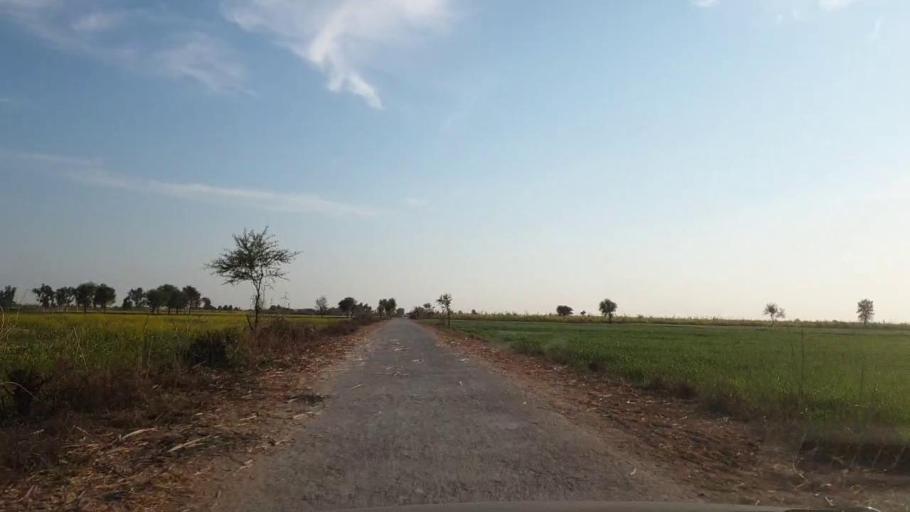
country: PK
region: Sindh
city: Khadro
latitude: 26.1780
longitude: 68.7527
